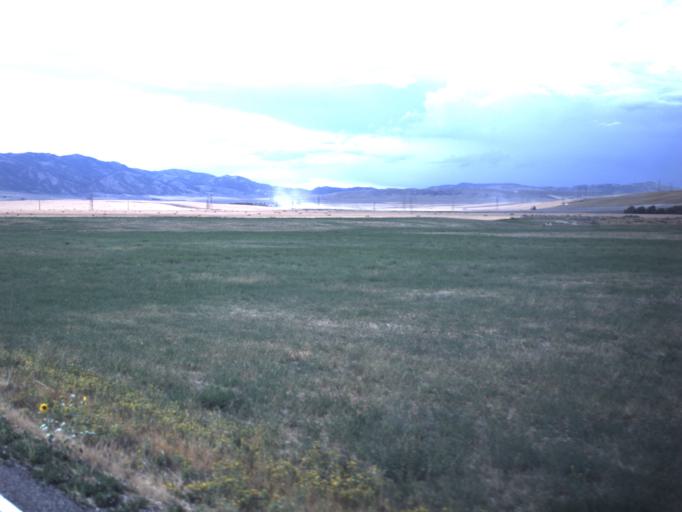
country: US
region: Utah
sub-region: Cache County
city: Lewiston
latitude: 41.9175
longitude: -111.9783
